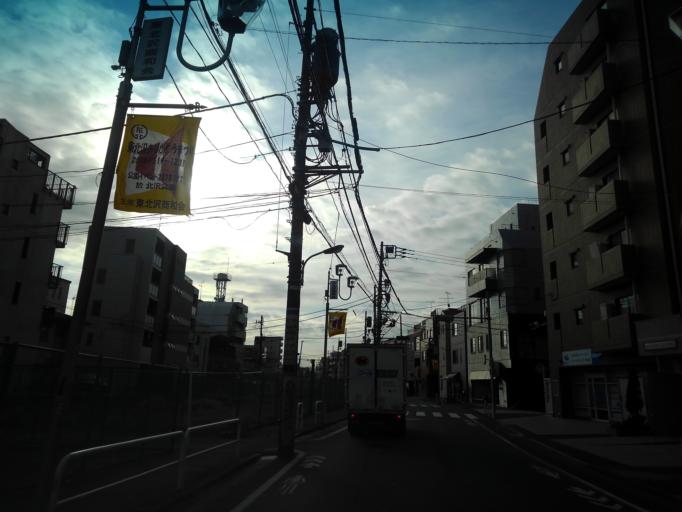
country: JP
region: Tokyo
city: Tokyo
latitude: 35.6677
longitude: 139.6730
